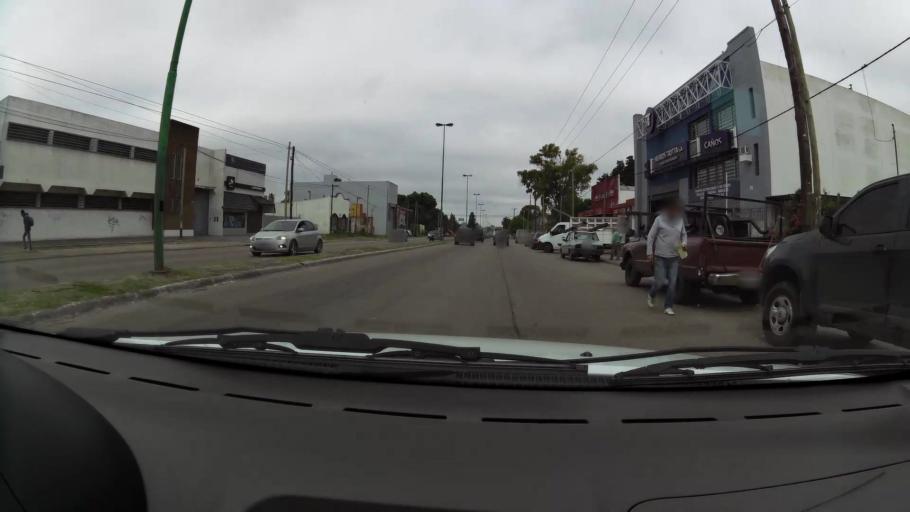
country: AR
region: Buenos Aires
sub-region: Partido de La Plata
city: La Plata
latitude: -34.9485
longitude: -57.9966
